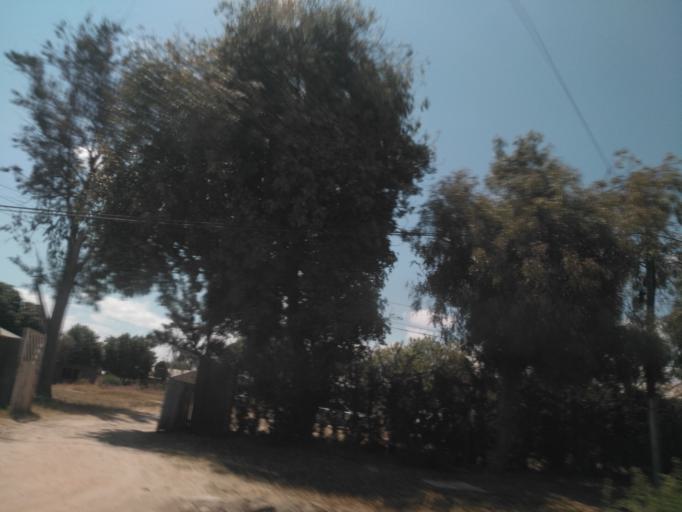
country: TZ
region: Dodoma
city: Dodoma
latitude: -6.1680
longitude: 35.7632
